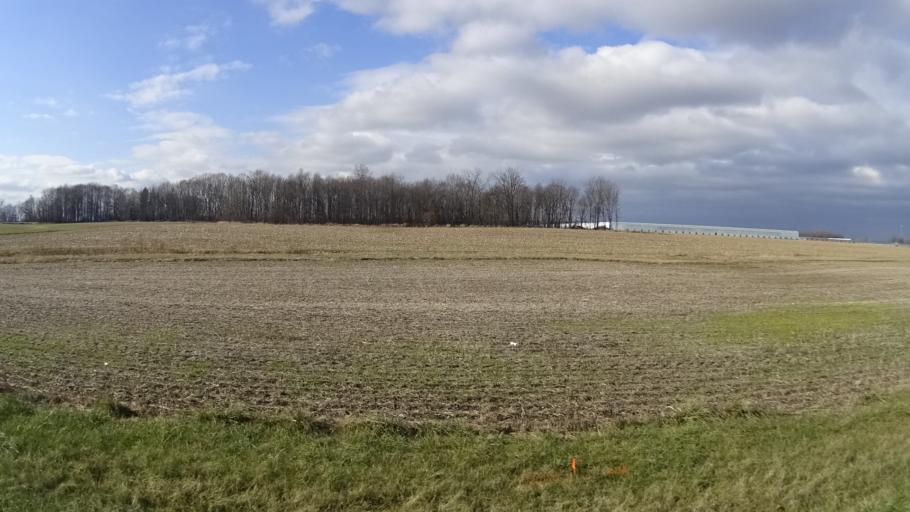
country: US
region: Ohio
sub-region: Lorain County
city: Camden
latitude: 41.2498
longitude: -82.2893
